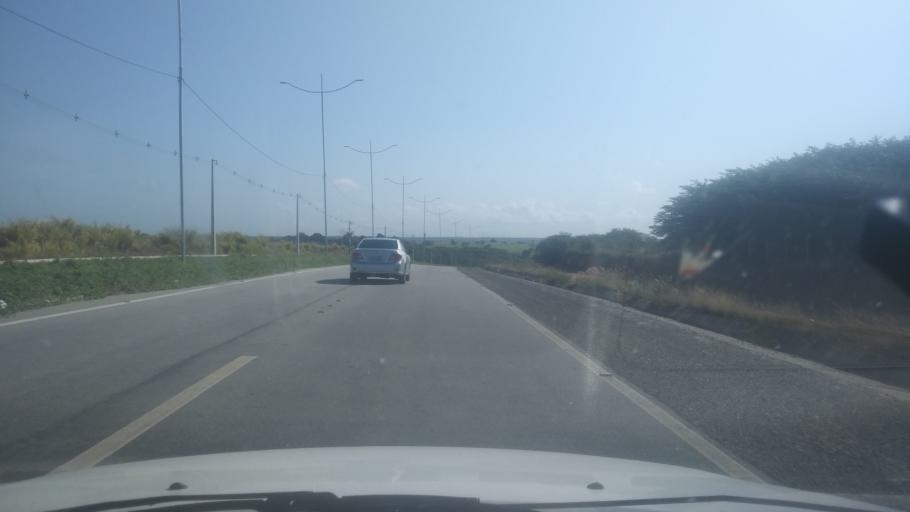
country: BR
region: Rio Grande do Norte
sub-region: Macaiba
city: Macaiba
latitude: -5.8386
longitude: -35.3750
